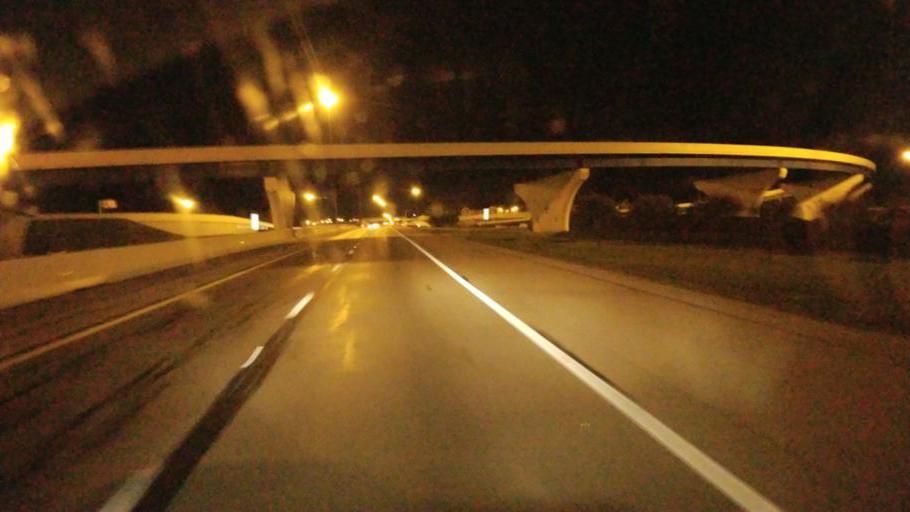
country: US
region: Ohio
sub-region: Montgomery County
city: Vandalia
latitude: 39.8657
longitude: -84.1861
